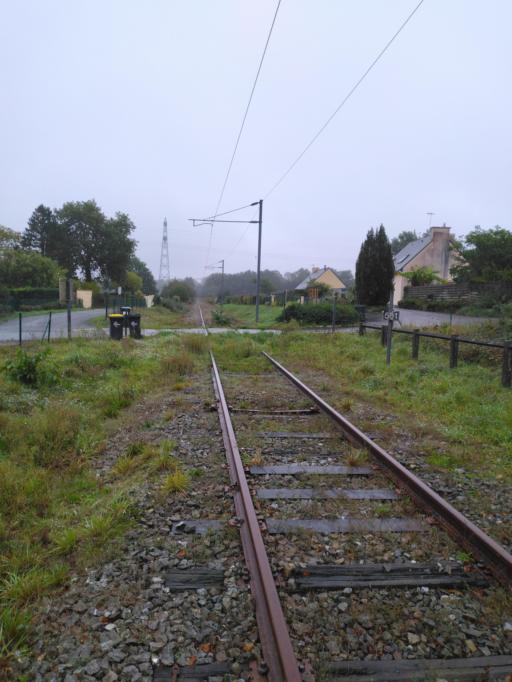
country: FR
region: Brittany
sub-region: Departement du Finistere
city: Melgven
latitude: 47.9353
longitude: -3.8850
